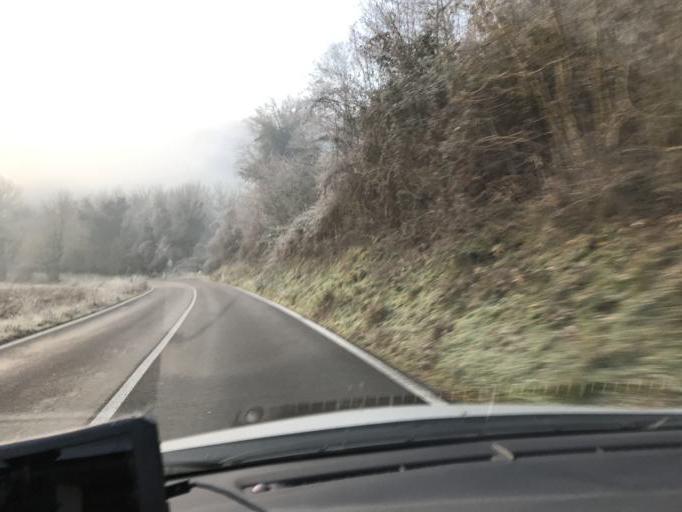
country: IT
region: Latium
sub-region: Provincia di Rieti
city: Colli sul Velino
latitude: 42.5210
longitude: 12.7341
